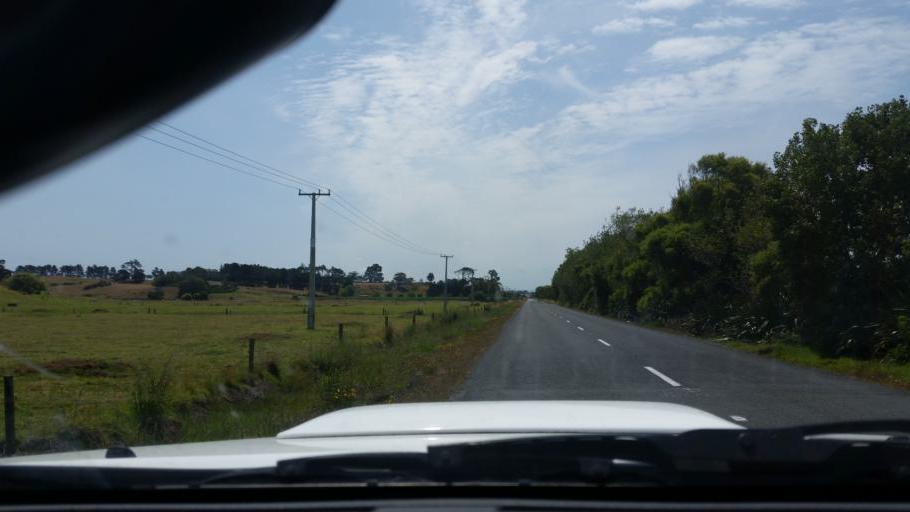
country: NZ
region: Northland
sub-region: Kaipara District
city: Dargaville
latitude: -36.0663
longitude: 173.9397
